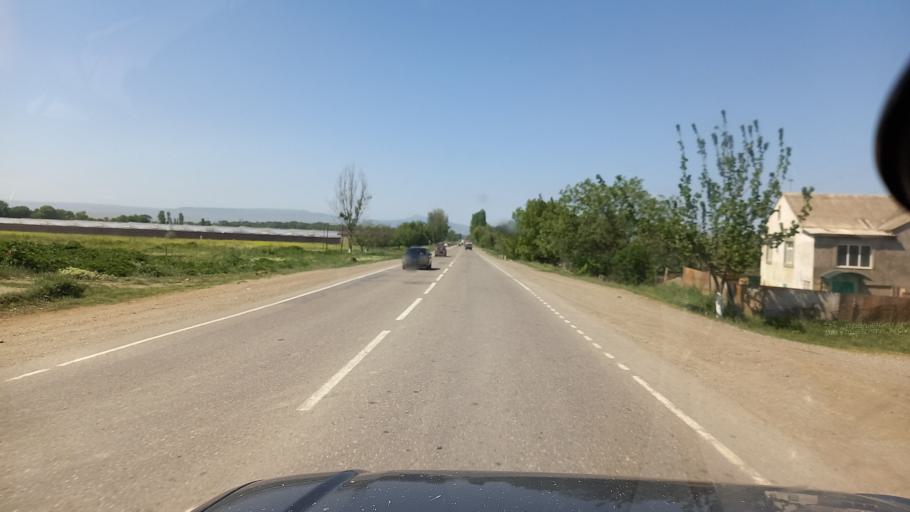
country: RU
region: Dagestan
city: Novaya Maka
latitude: 41.8289
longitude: 48.3872
